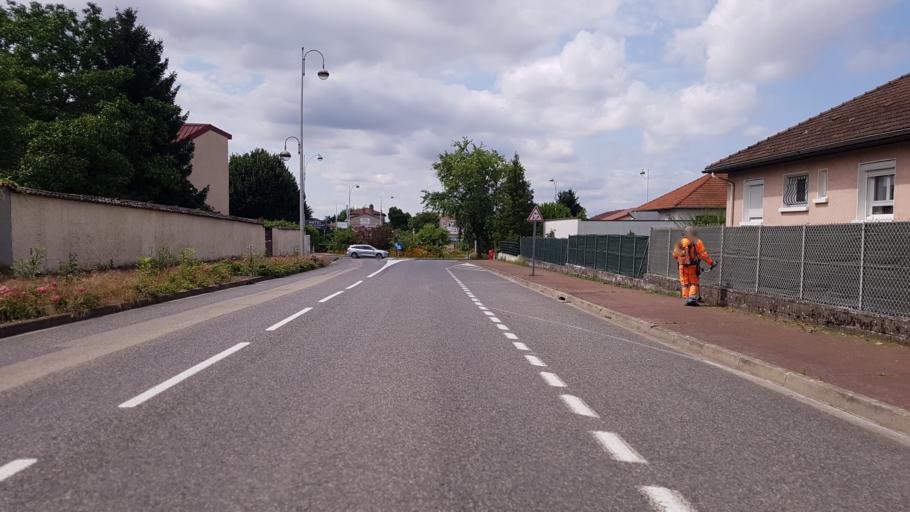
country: FR
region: Rhone-Alpes
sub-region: Departement du Rhone
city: Genas
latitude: 45.7338
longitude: 4.9932
